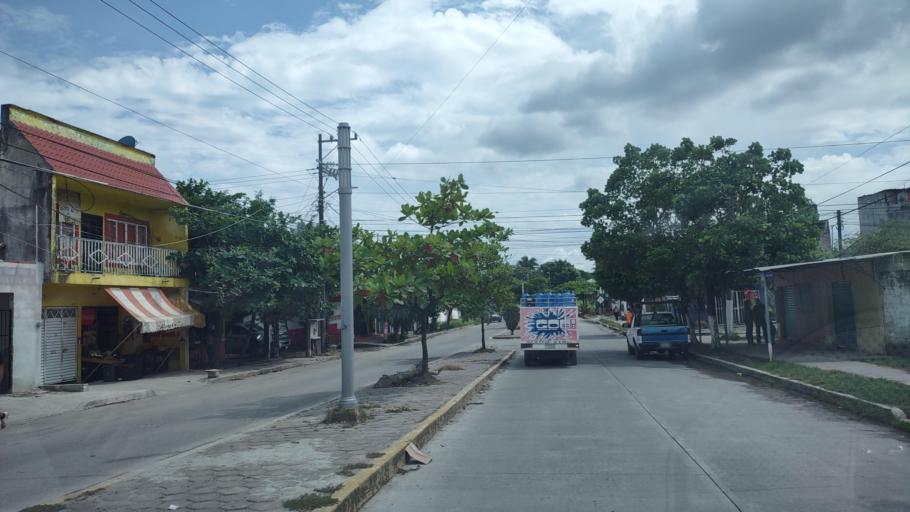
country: MX
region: Veracruz
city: Martinez de la Torre
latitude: 20.0719
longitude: -97.0754
